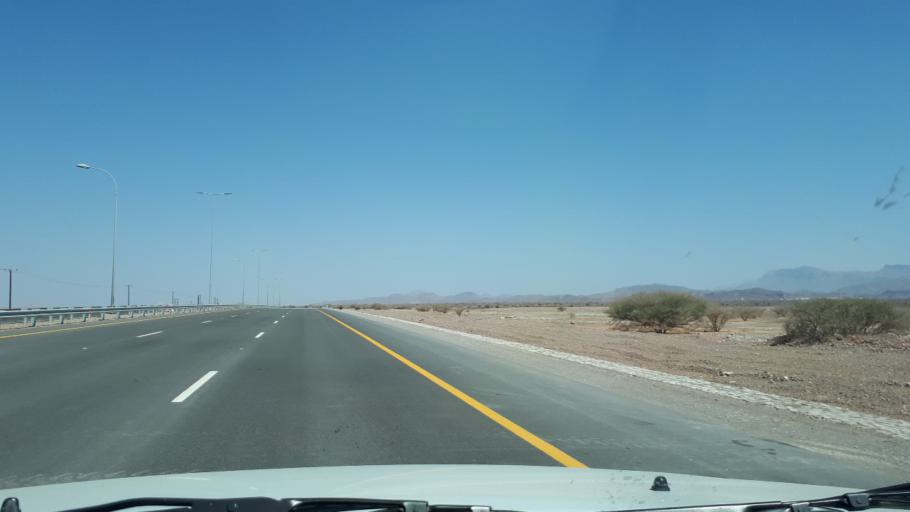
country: OM
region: Ash Sharqiyah
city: Badiyah
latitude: 22.4113
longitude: 59.0569
